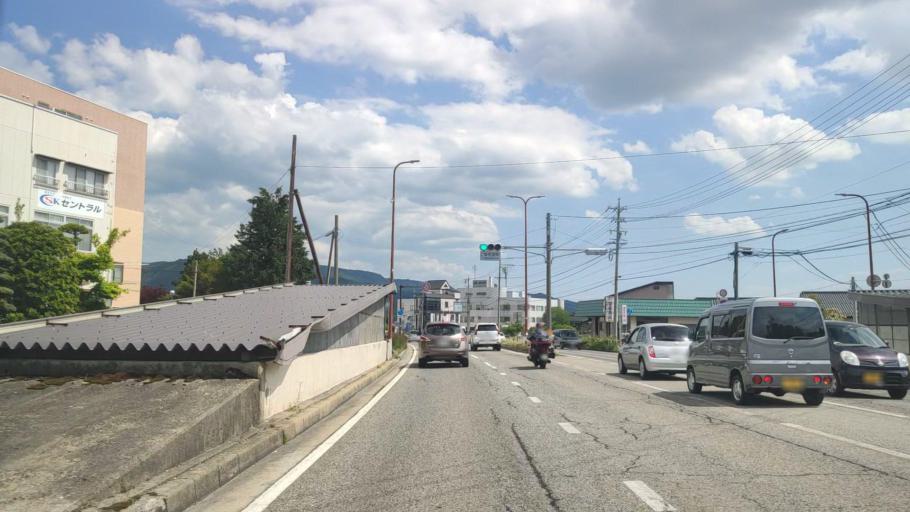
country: JP
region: Nagano
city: Omachi
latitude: 36.5014
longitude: 137.8562
